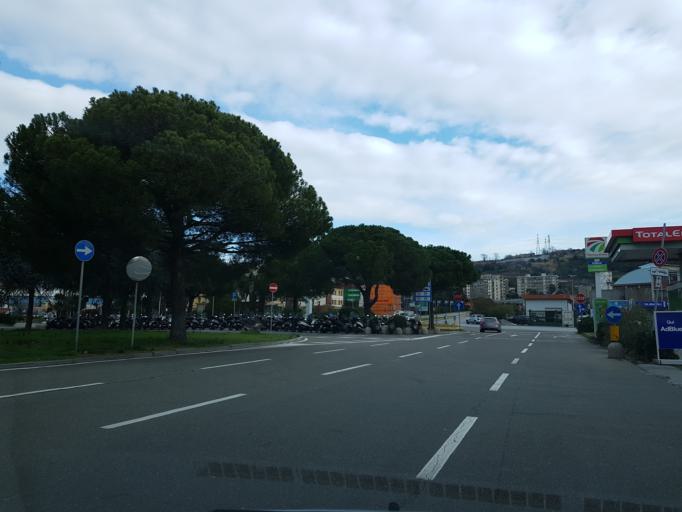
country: IT
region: Liguria
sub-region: Provincia di Genova
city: San Teodoro
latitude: 44.4161
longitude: 8.8539
